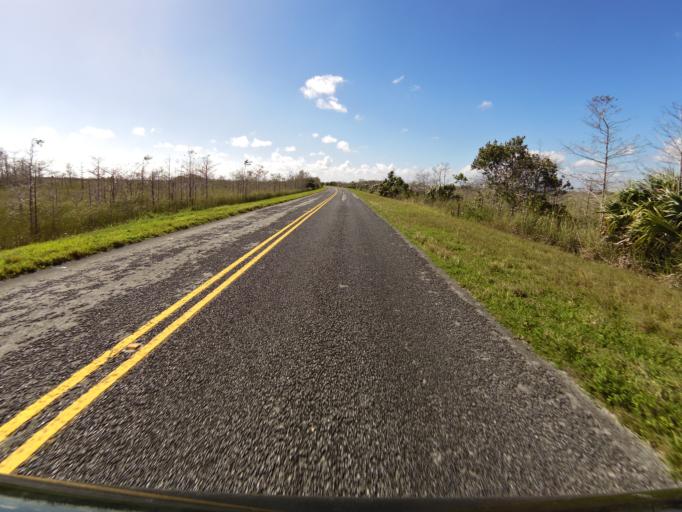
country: US
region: Florida
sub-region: Miami-Dade County
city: Florida City
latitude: 25.4302
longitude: -80.7672
